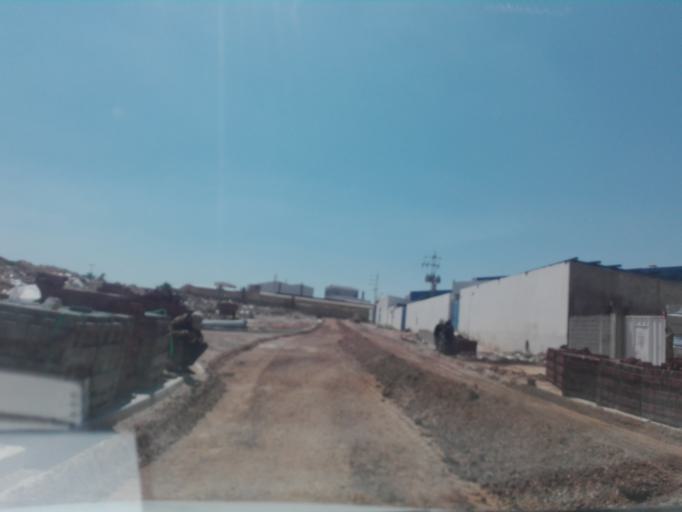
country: TN
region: Safaqis
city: Sfax
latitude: 34.7268
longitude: 10.5170
